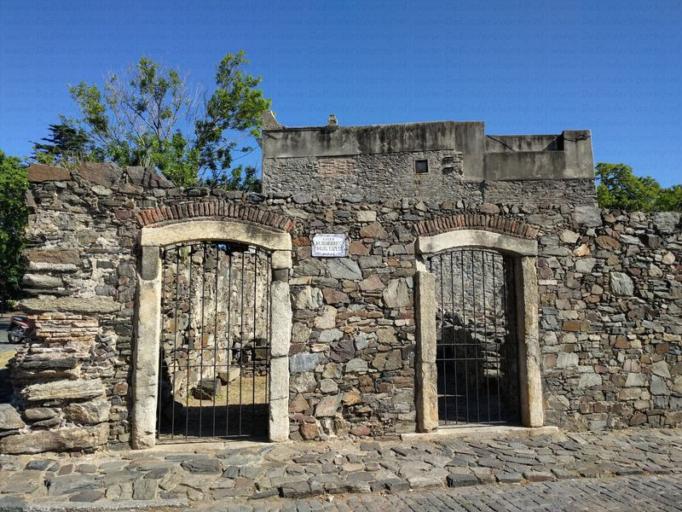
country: UY
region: Colonia
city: Colonia del Sacramento
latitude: -34.4720
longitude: -57.8525
